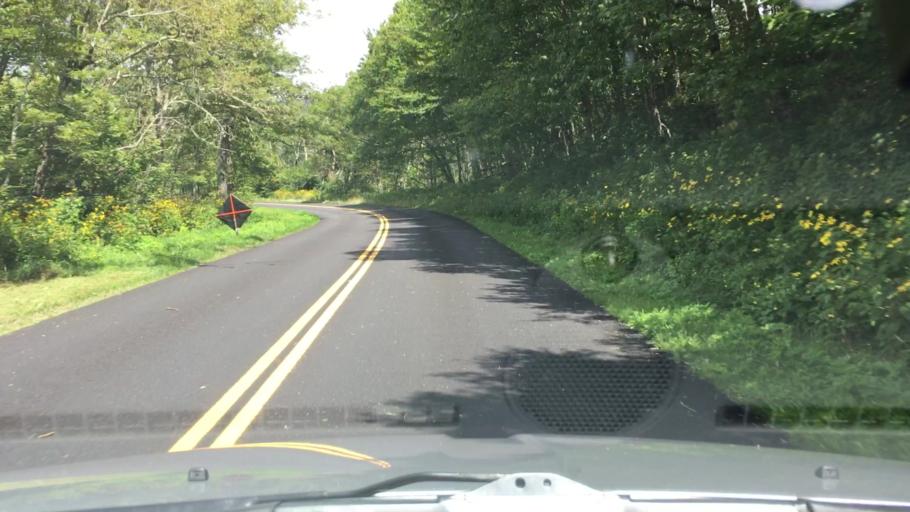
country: US
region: North Carolina
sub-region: Buncombe County
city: Black Mountain
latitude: 35.7417
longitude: -82.3394
